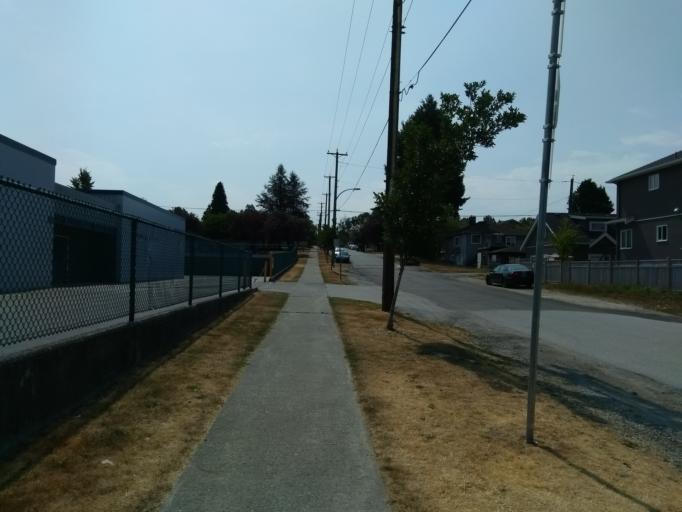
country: CA
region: British Columbia
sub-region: Fraser Valley Regional District
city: North Vancouver
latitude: 49.2470
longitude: -123.0390
